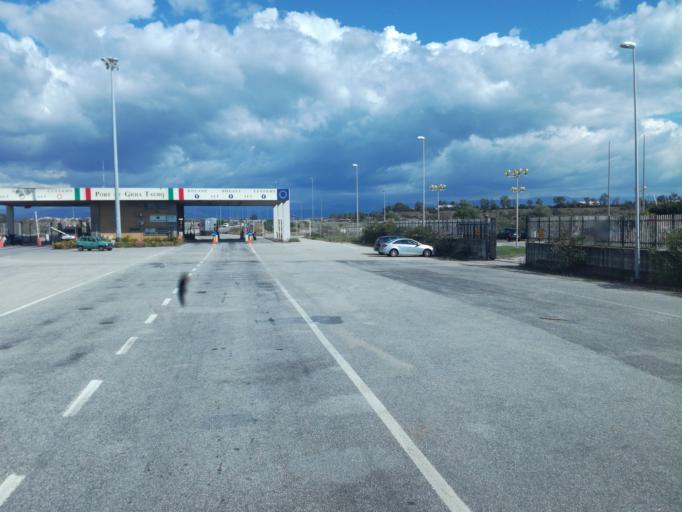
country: IT
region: Calabria
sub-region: Provincia di Reggio Calabria
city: San Ferdinando
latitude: 38.4812
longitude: 15.9282
